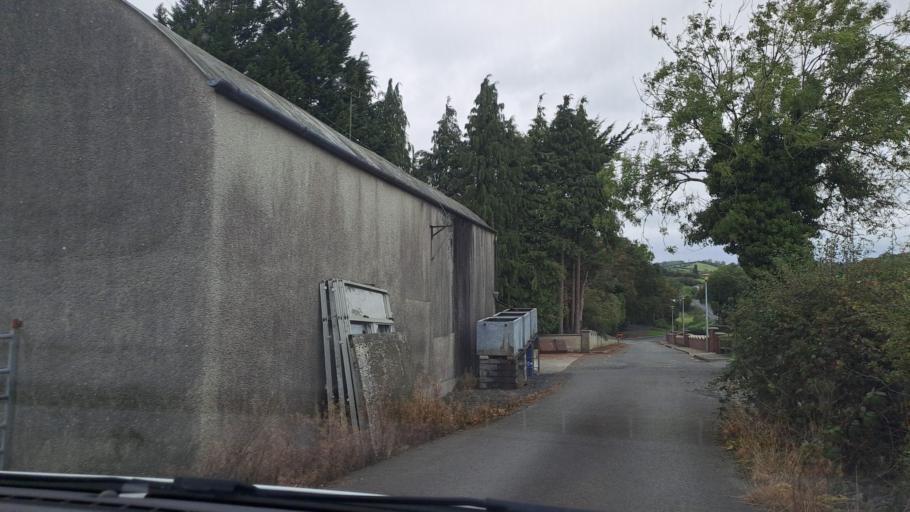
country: IE
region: Ulster
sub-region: An Cabhan
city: Bailieborough
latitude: 54.0091
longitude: -6.9197
